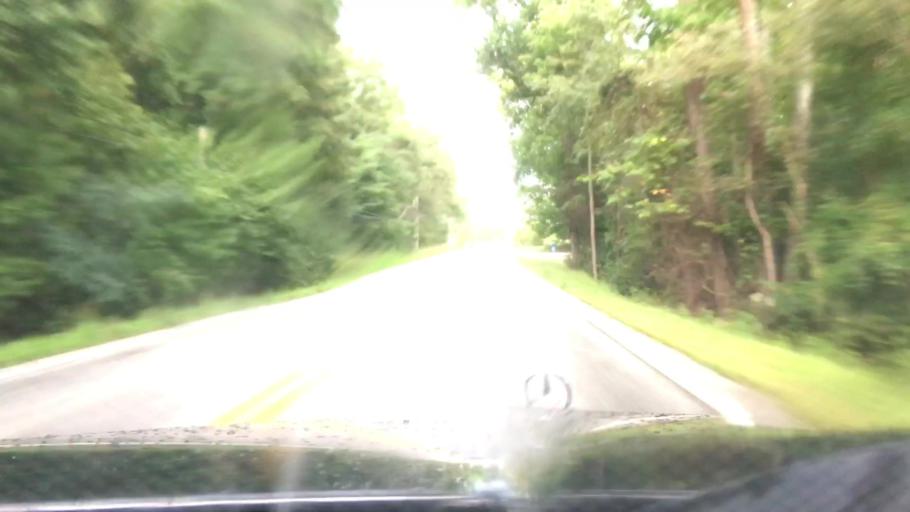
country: US
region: Virginia
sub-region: Nelson County
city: Lovingston
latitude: 37.7660
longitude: -78.9788
